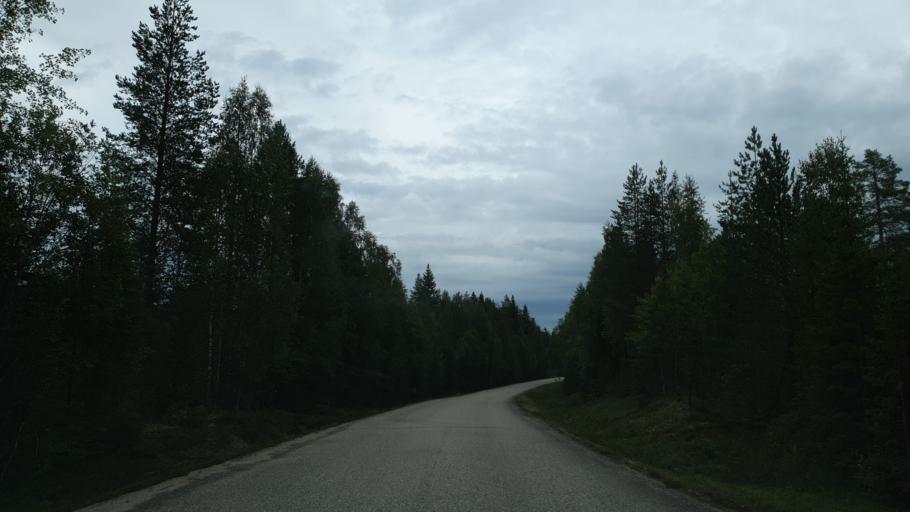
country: FI
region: Kainuu
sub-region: Kehys-Kainuu
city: Kuhmo
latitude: 64.3519
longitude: 29.1524
